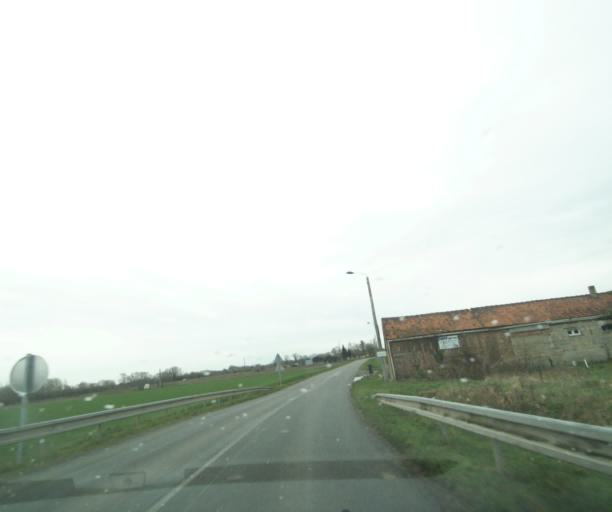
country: FR
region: Nord-Pas-de-Calais
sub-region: Departement du Nord
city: Crespin
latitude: 50.4340
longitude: 3.6611
